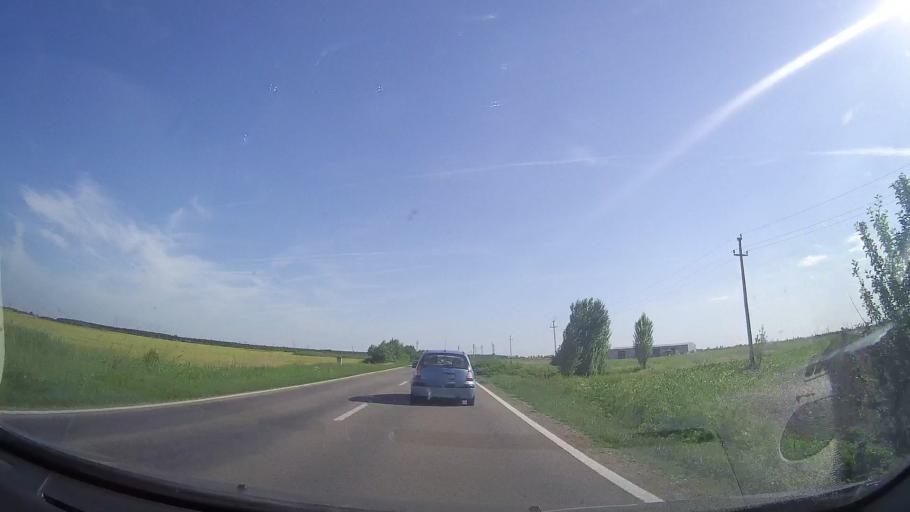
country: RO
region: Prahova
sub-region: Comuna Berceni
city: Berceni
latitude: 44.9294
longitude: 26.1035
